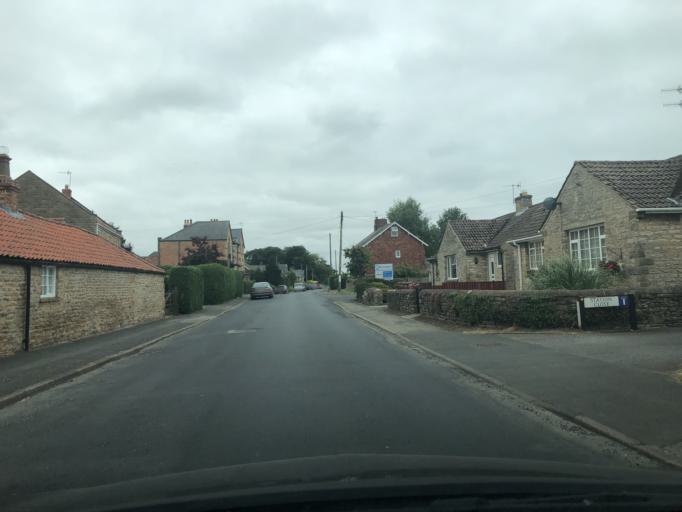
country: GB
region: England
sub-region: North Yorkshire
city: East Ayton
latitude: 54.2478
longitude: -0.4881
